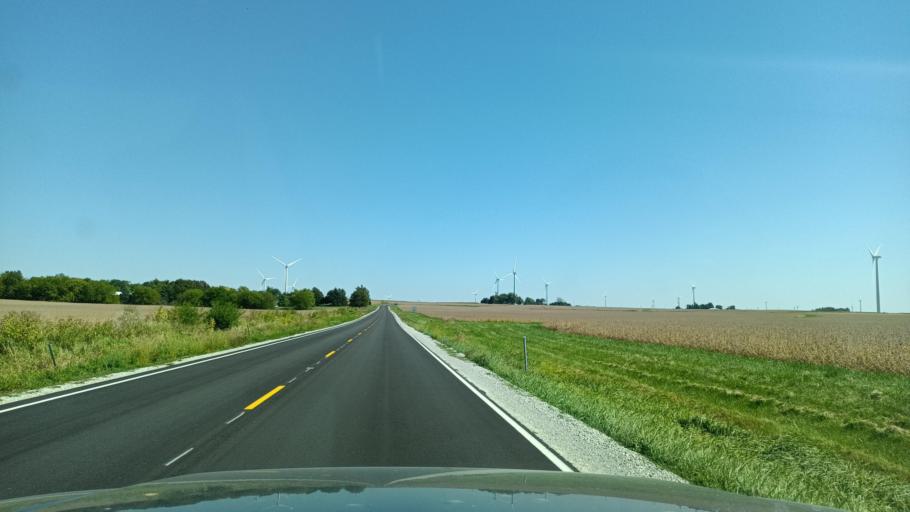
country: US
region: Illinois
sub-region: McLean County
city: Danvers
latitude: 40.5827
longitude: -89.1122
